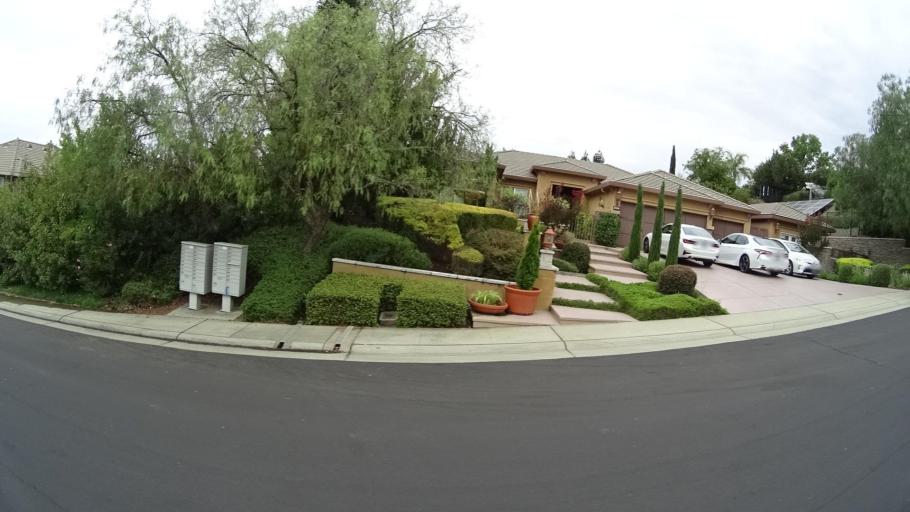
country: US
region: California
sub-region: Placer County
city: Rocklin
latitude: 38.7729
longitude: -121.2251
